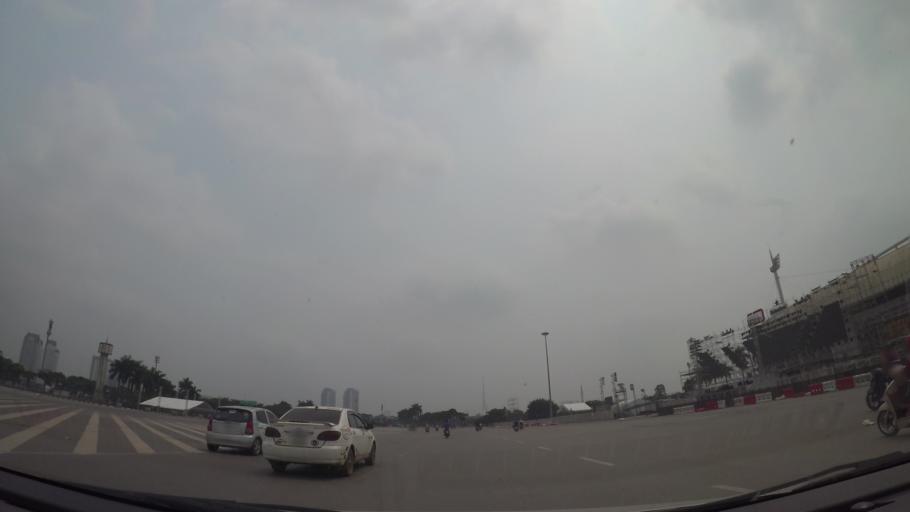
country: VN
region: Ha Noi
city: Cau Dien
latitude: 21.0209
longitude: 105.7662
